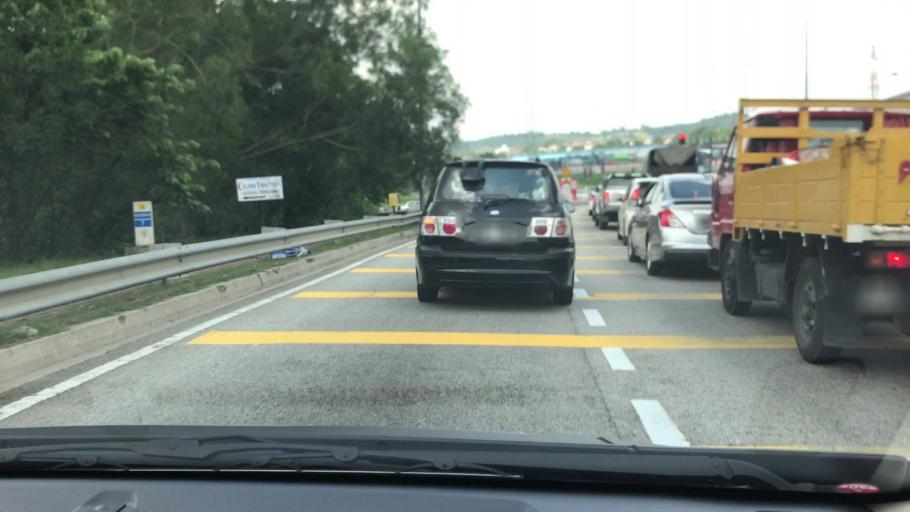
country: MY
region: Putrajaya
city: Putrajaya
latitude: 2.9848
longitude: 101.6634
